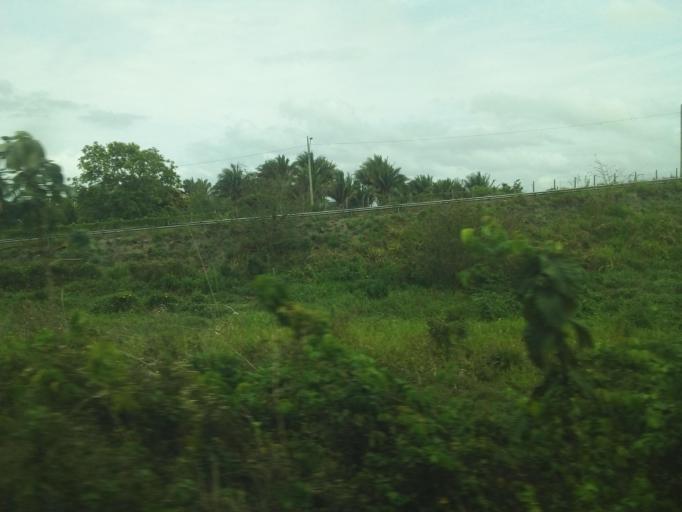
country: BR
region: Maranhao
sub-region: Itapecuru Mirim
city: Itapecuru Mirim
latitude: -3.3172
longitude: -44.4797
